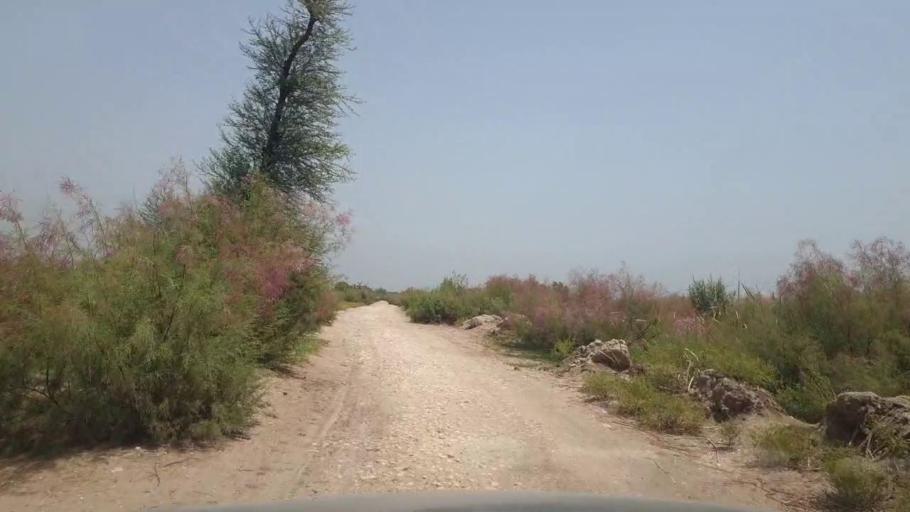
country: PK
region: Sindh
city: Garhi Yasin
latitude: 27.9505
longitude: 68.4328
